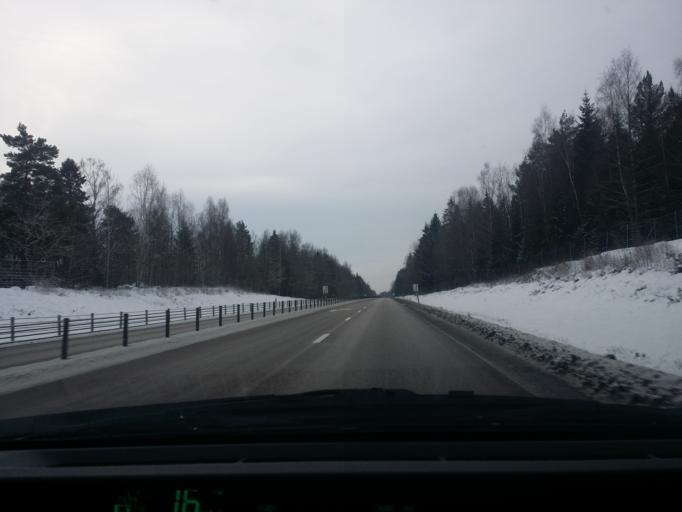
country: SE
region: Vaestra Goetaland
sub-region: Mariestads Kommun
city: Mariestad
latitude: 58.6086
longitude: 13.8036
